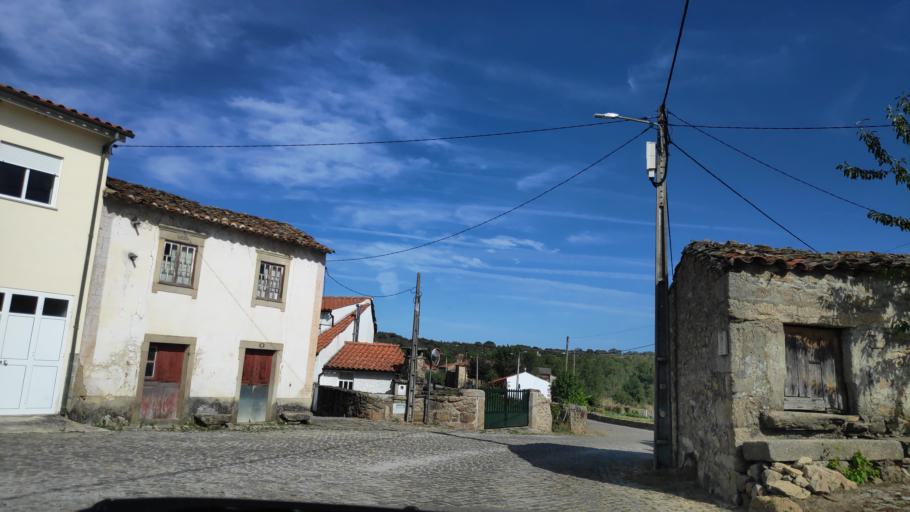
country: ES
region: Castille and Leon
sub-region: Provincia de Zamora
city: Fariza
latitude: 41.4290
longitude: -6.3452
